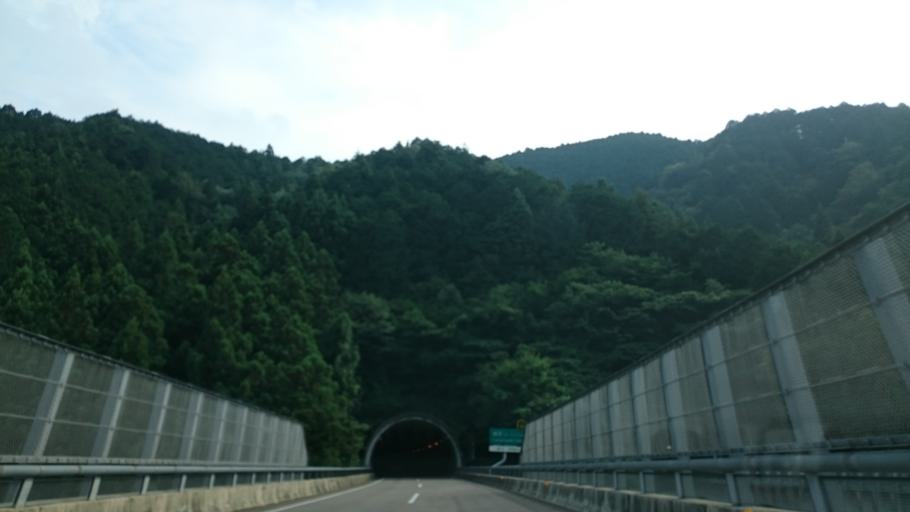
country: JP
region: Gifu
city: Mino
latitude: 35.5973
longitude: 136.9449
